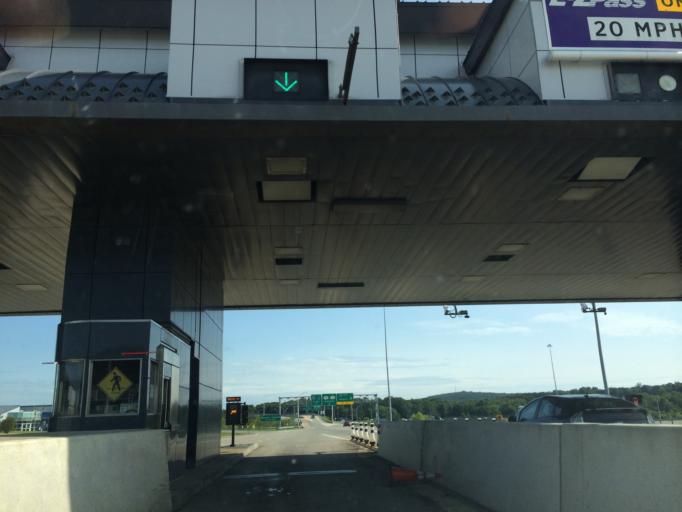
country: US
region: New York
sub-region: Orange County
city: Gardnertown
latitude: 41.5108
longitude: -74.0704
